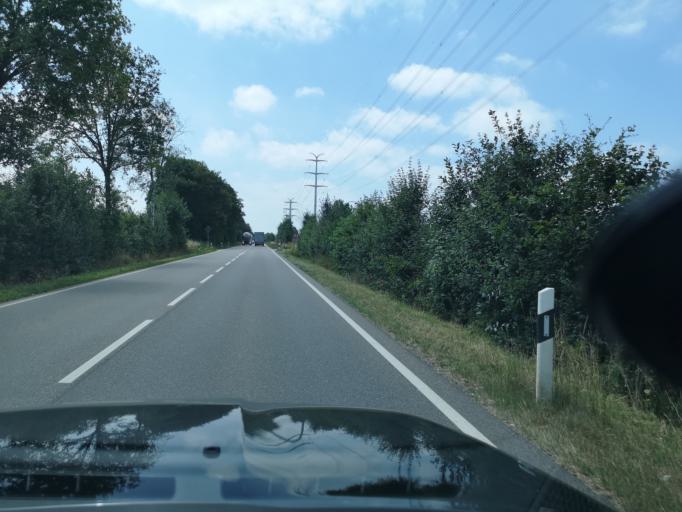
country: DE
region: North Rhine-Westphalia
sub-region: Regierungsbezirk Munster
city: Isselburg
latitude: 51.8299
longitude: 6.4492
